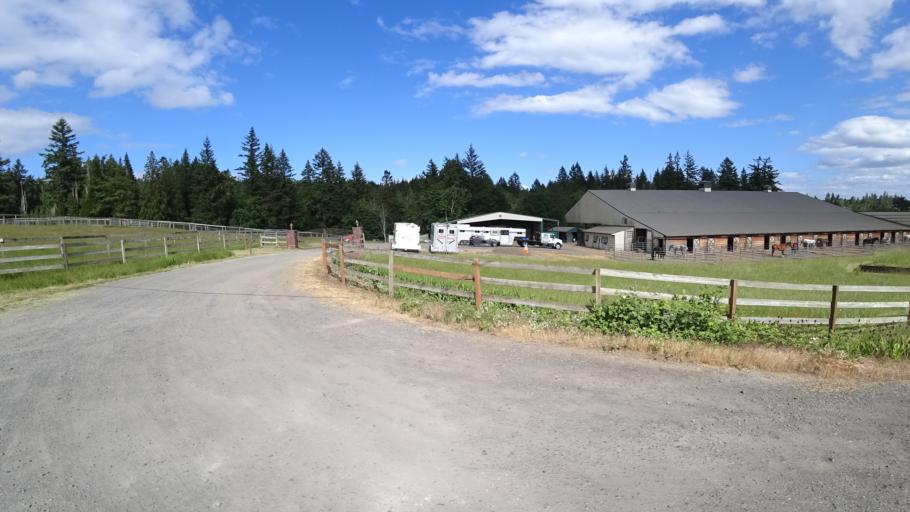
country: US
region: Oregon
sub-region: Washington County
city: Bethany
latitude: 45.5832
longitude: -122.8407
